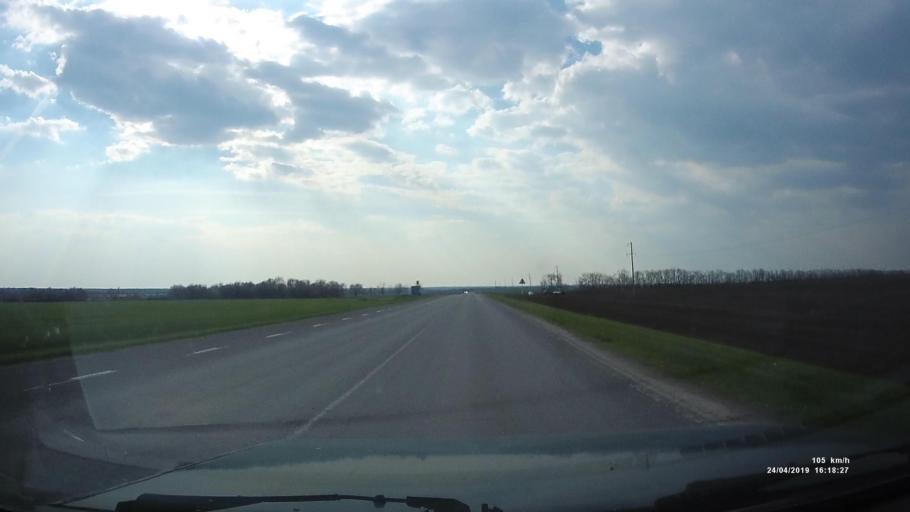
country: RU
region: Rostov
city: Sovetskoye
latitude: 46.7745
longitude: 42.1160
